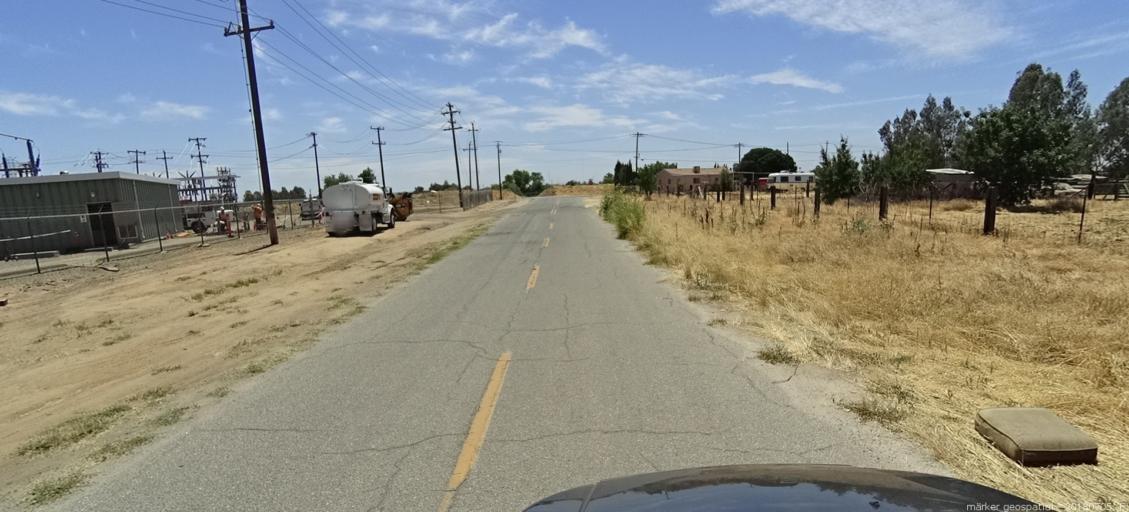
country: US
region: California
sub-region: Madera County
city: Madera
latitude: 36.9833
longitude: -120.0342
